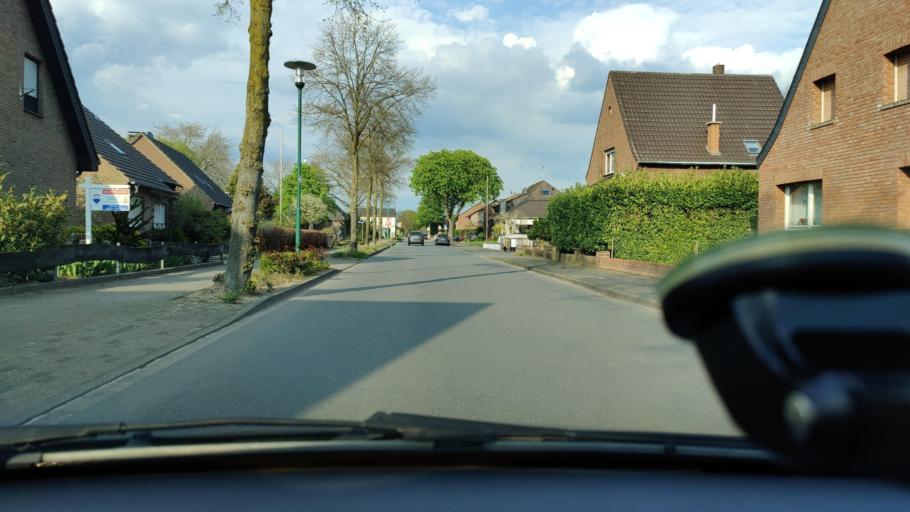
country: DE
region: North Rhine-Westphalia
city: Rees
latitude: 51.7226
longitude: 6.3507
